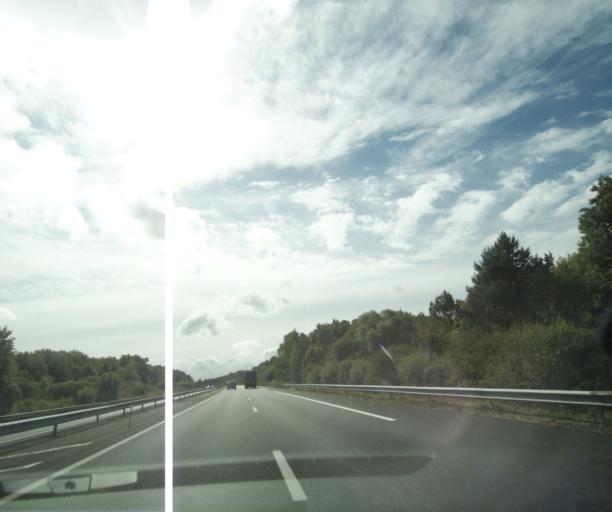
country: FR
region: Poitou-Charentes
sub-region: Departement de la Charente-Maritime
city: Thenac
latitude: 45.6467
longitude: -0.6310
